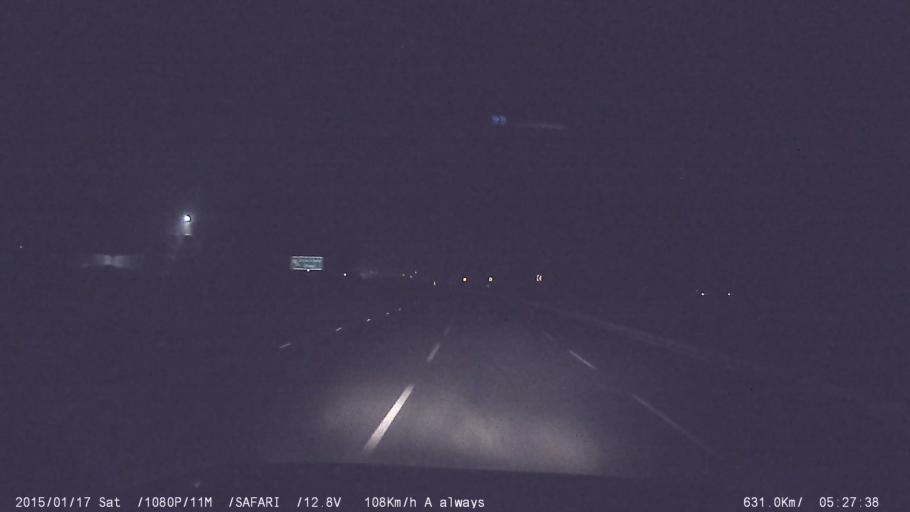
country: IN
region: Tamil Nadu
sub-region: Vellore
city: Arcot
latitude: 12.9304
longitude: 79.2620
